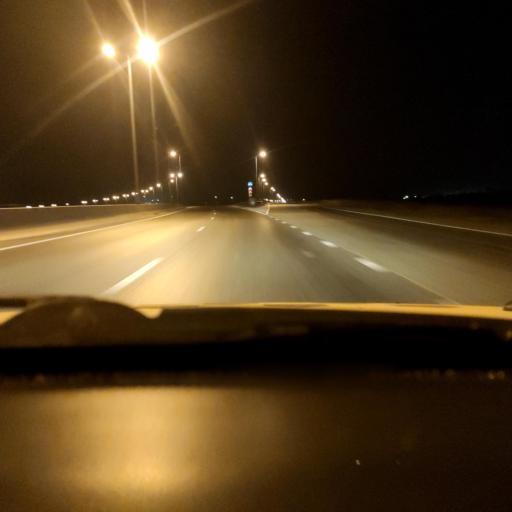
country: RU
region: Perm
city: Kondratovo
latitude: 57.9321
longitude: 56.1647
